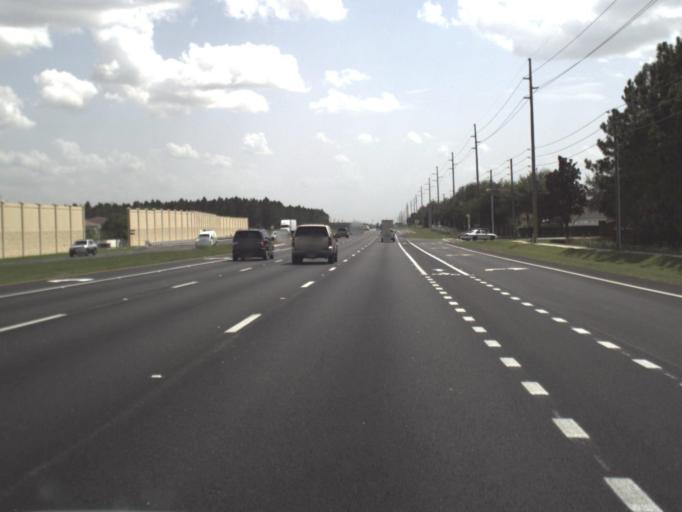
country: US
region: Florida
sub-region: Lake County
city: Four Corners
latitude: 28.2679
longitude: -81.6609
